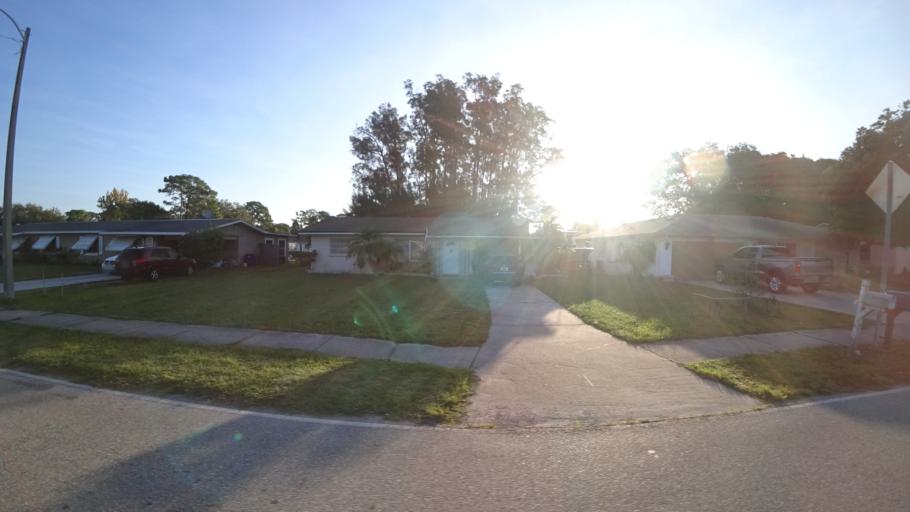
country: US
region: Florida
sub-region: Manatee County
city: South Bradenton
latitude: 27.4539
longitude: -82.5820
